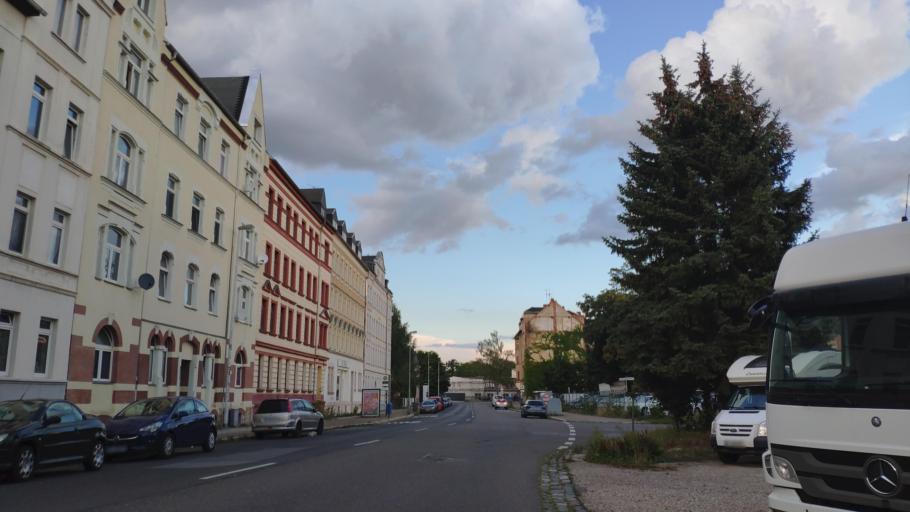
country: DE
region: Saxony
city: Chemnitz
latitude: 50.8157
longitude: 12.9112
